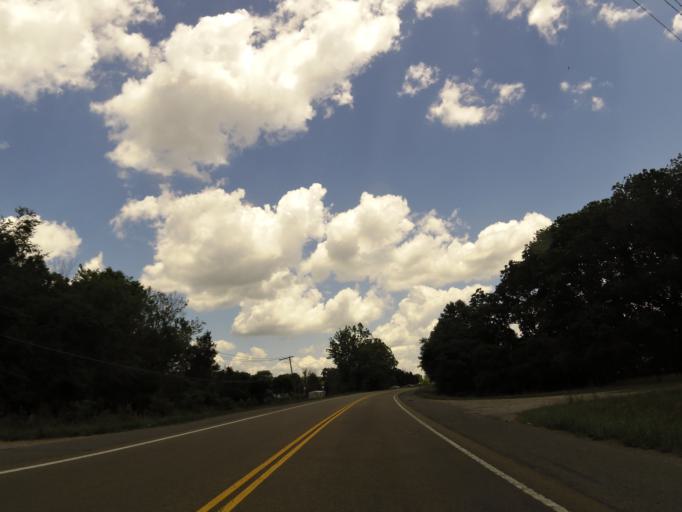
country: US
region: Tennessee
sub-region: Union County
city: Condon
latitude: 36.2078
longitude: -83.8732
